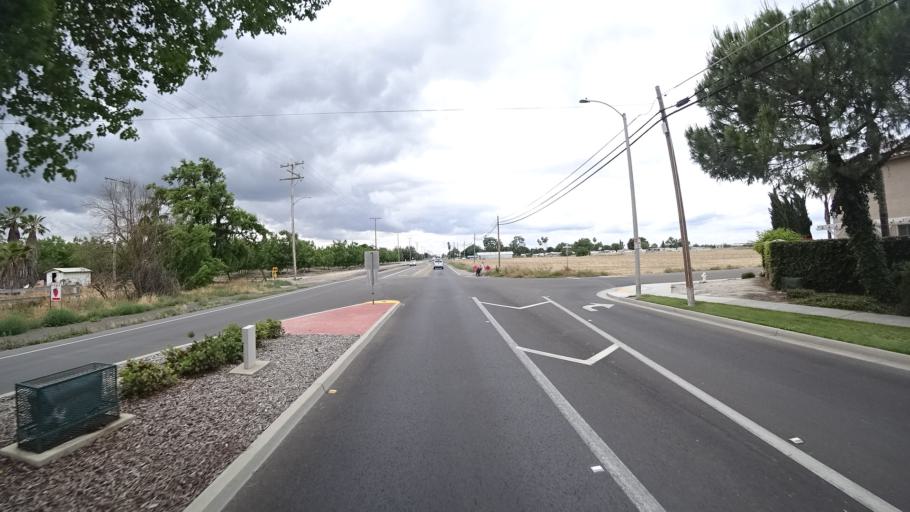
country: US
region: California
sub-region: Kings County
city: Armona
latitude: 36.3281
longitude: -119.6837
